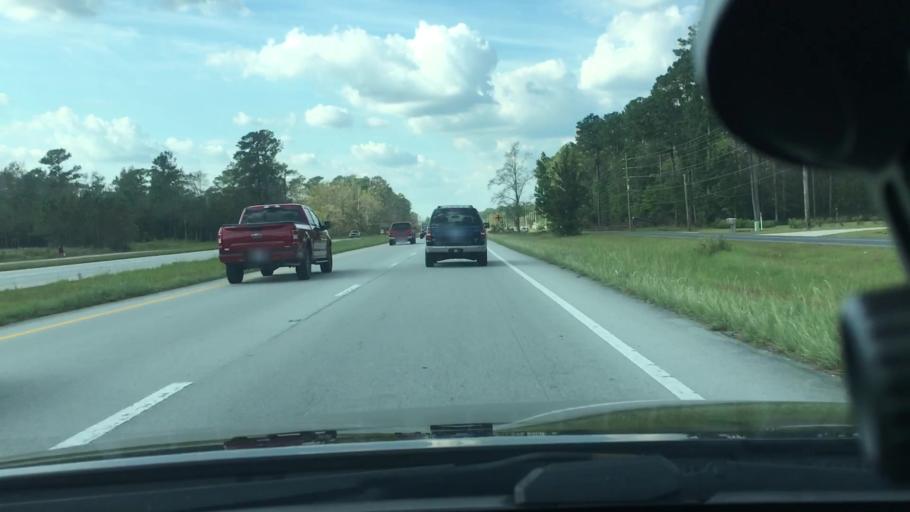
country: US
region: North Carolina
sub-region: Craven County
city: Neuse Forest
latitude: 35.0000
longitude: -76.9864
